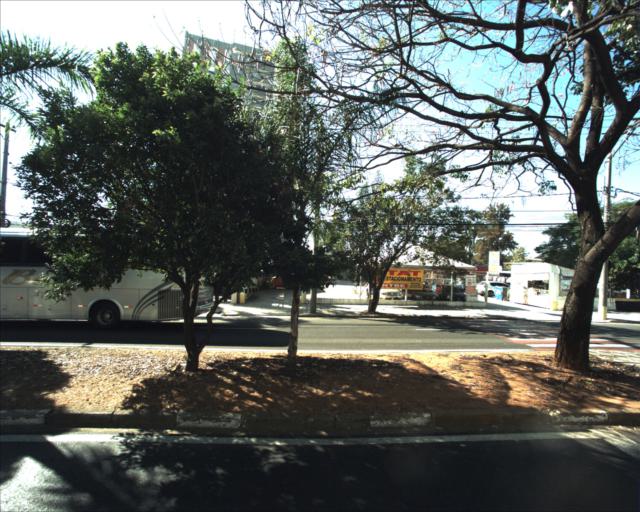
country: BR
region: Sao Paulo
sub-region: Sorocaba
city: Sorocaba
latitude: -23.5096
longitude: -47.4558
